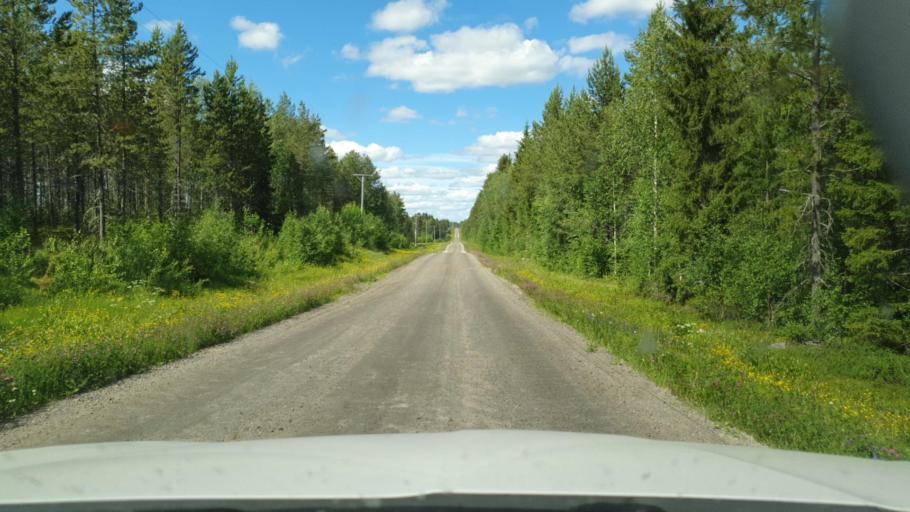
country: SE
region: Vaesterbotten
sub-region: Skelleftea Kommun
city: Backa
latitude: 65.1693
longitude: 21.1167
